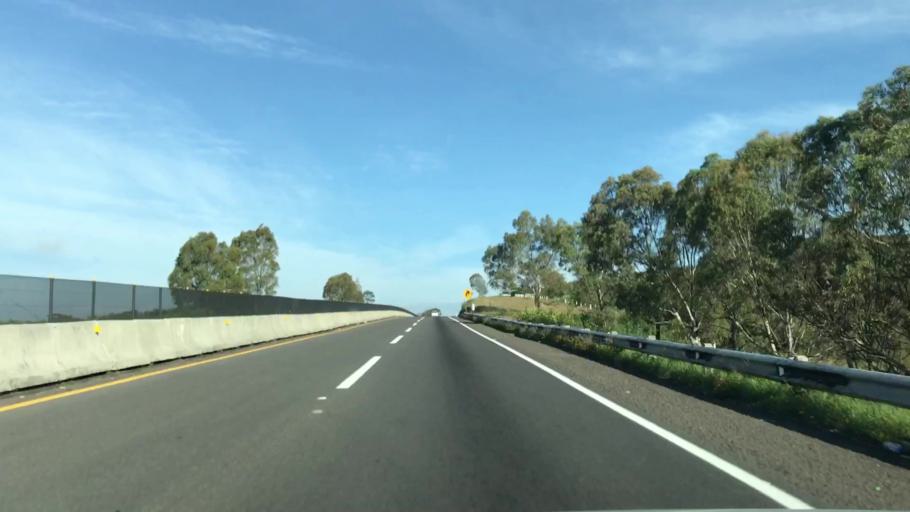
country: MX
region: Jalisco
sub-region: Lagos de Moreno
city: Cristeros [Fraccionamiento]
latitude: 21.3696
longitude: -102.1303
